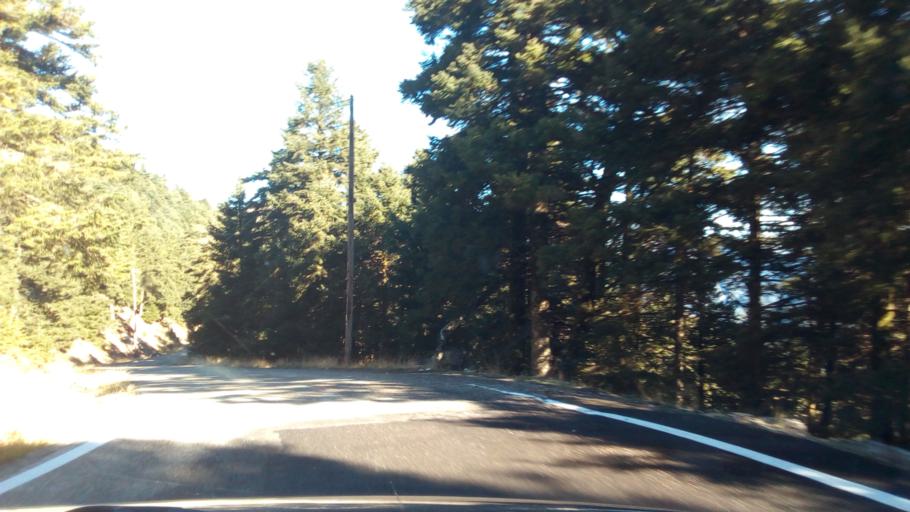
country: GR
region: West Greece
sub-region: Nomos Aitolias kai Akarnanias
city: Nafpaktos
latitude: 38.5336
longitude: 21.8415
